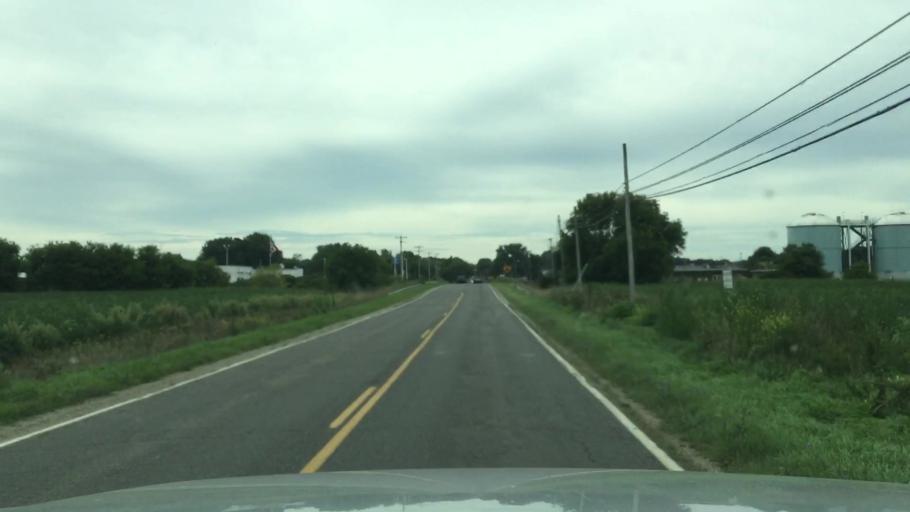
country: US
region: Michigan
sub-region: Shiawassee County
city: Durand
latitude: 42.9287
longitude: -83.9883
